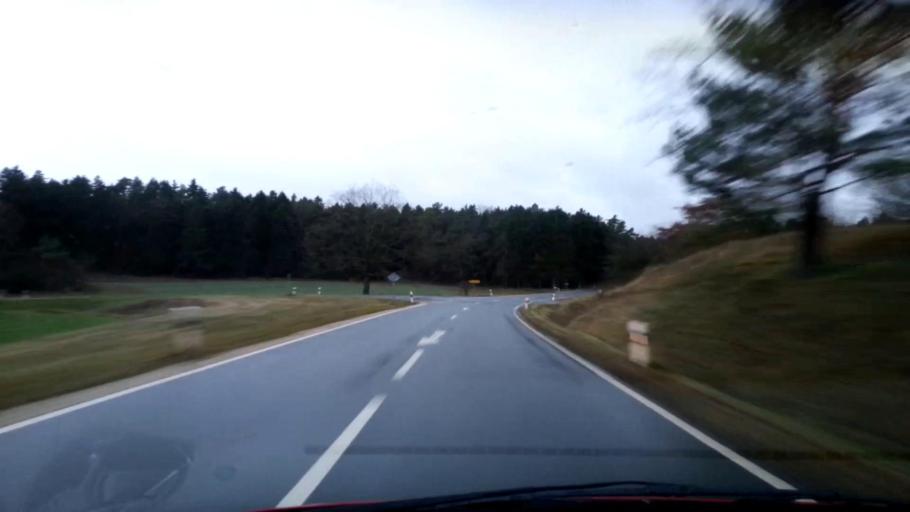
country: DE
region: Bavaria
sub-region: Upper Franconia
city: Konigsfeld
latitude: 49.9419
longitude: 11.1907
